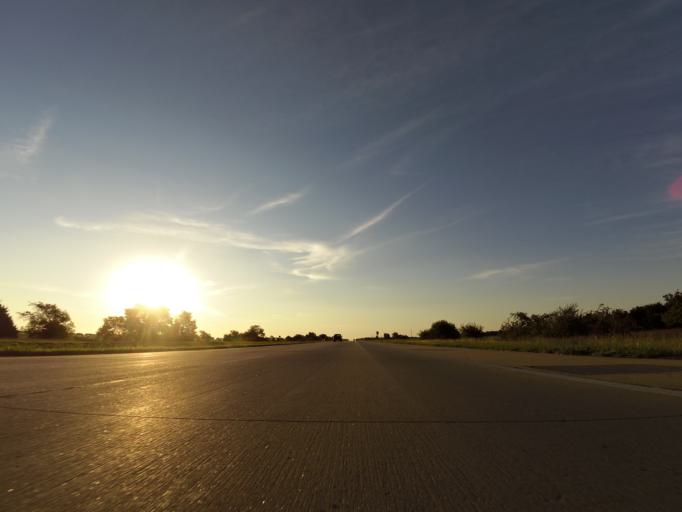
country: US
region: Kansas
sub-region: Reno County
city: Haven
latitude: 37.8917
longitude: -97.7581
